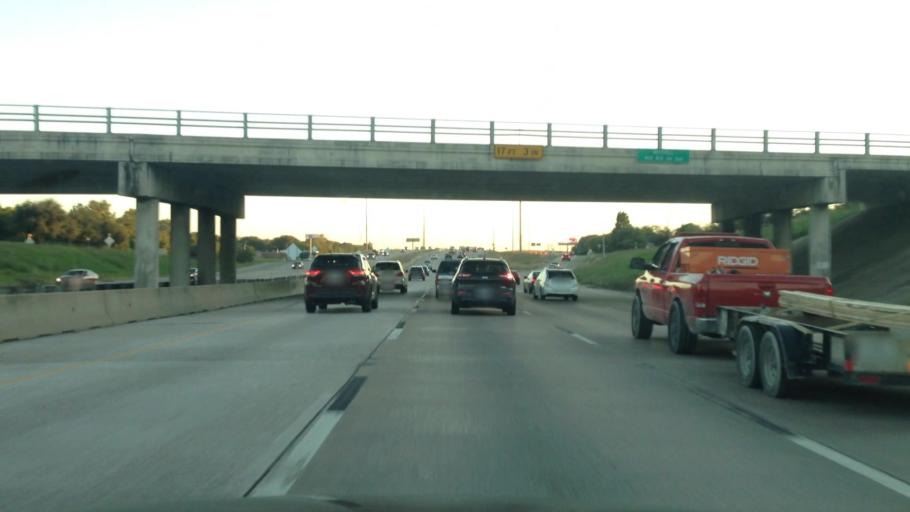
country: US
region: Texas
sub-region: Tarrant County
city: Arlington
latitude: 32.7261
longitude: -97.0626
